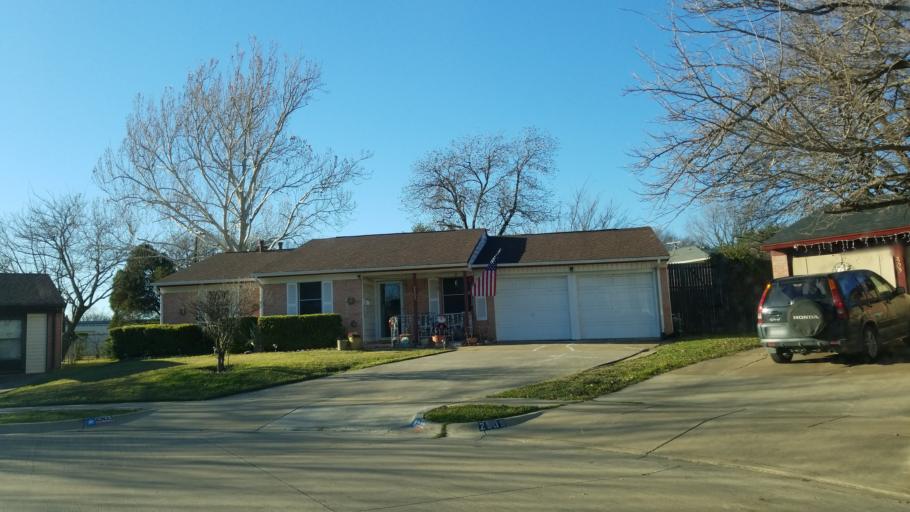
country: US
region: Texas
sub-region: Tarrant County
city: Arlington
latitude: 32.7315
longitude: -97.0640
